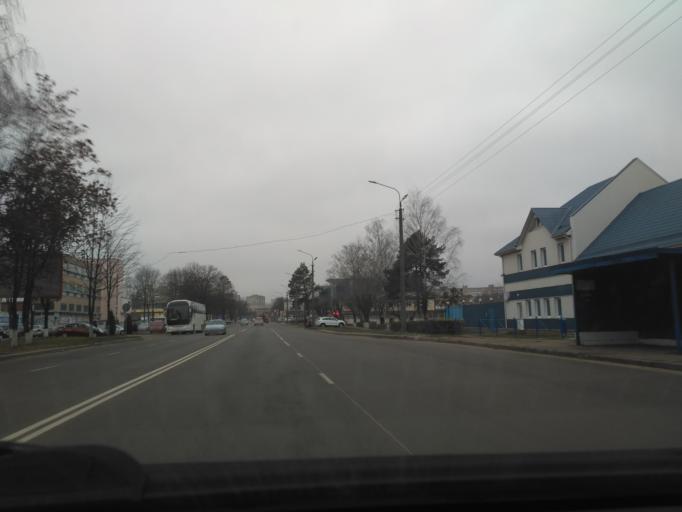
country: BY
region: Minsk
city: Horad Barysaw
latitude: 54.2074
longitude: 28.4941
